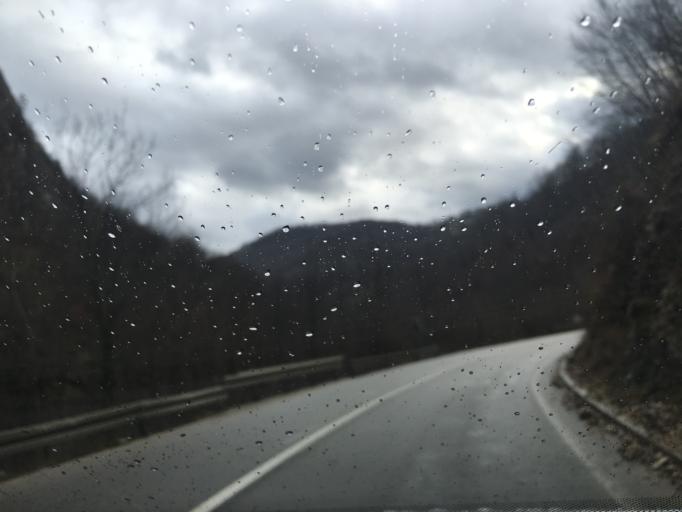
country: RS
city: Sokolovo Brdo
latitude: 43.2033
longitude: 19.7638
